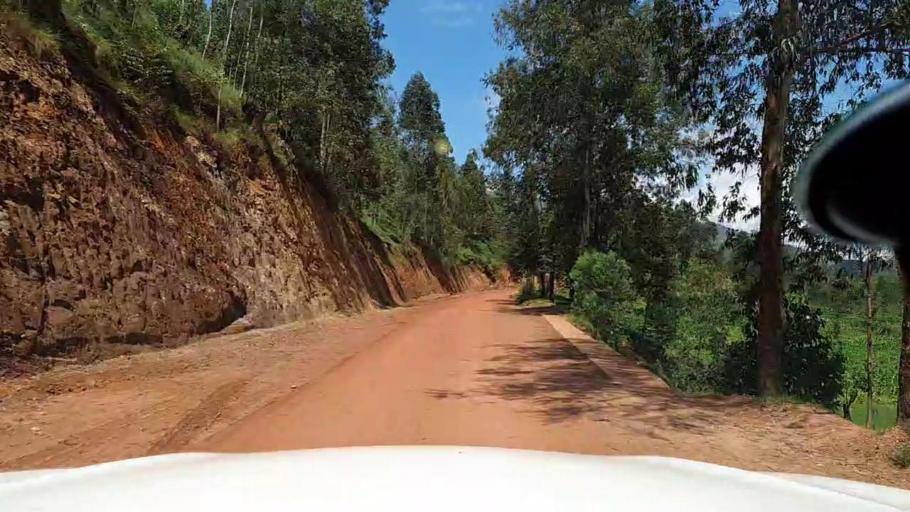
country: RW
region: Kigali
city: Kigali
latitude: -1.7840
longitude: 29.8806
